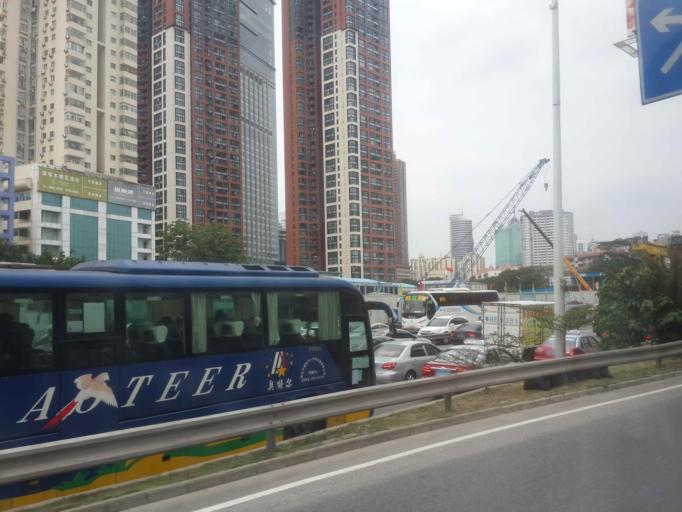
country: CN
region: Guangdong
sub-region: Shenzhen
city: Shenzhen
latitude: 22.5380
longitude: 114.1033
